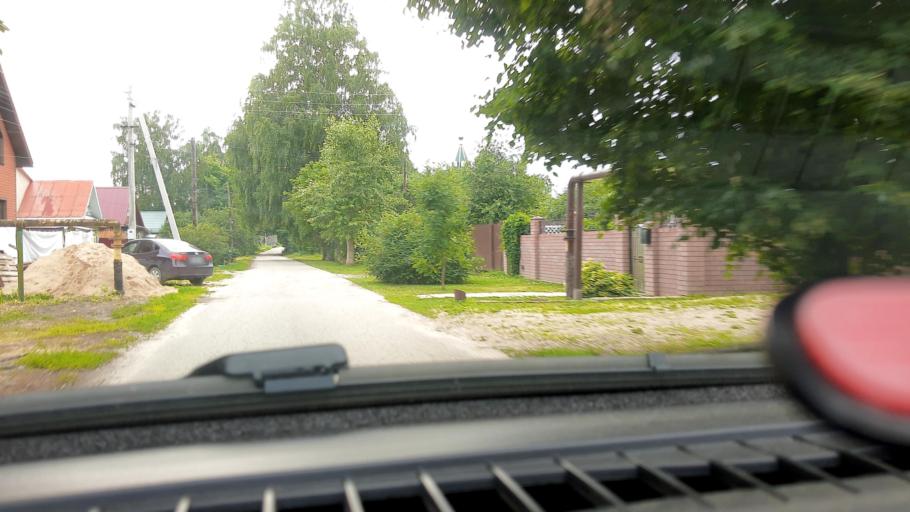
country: RU
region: Nizjnij Novgorod
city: Gorodets
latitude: 56.6339
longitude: 43.4729
